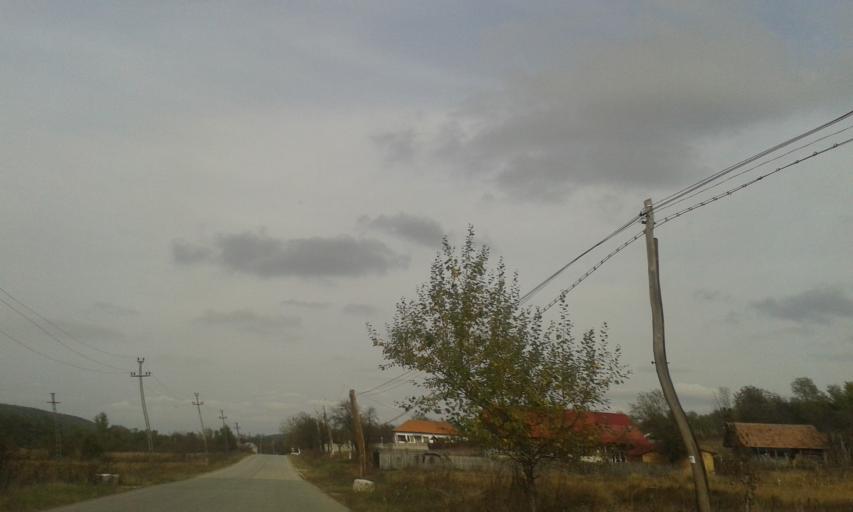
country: RO
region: Gorj
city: Logresti
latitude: 44.8634
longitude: 23.7012
